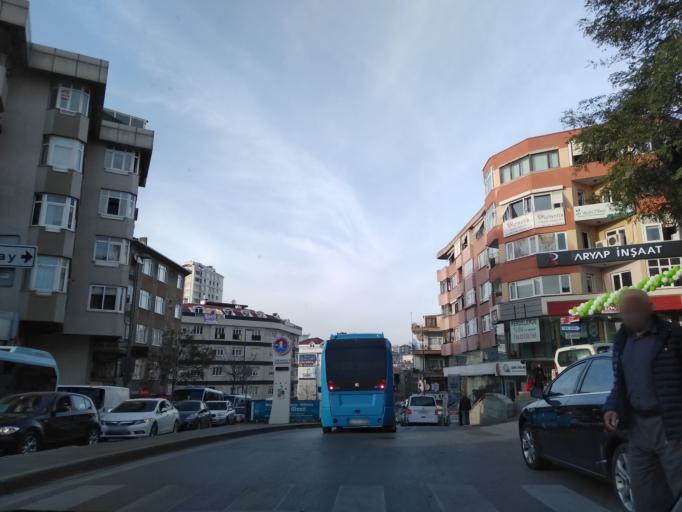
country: TR
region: Istanbul
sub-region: Atasehir
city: Atasehir
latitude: 40.9528
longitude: 29.1009
